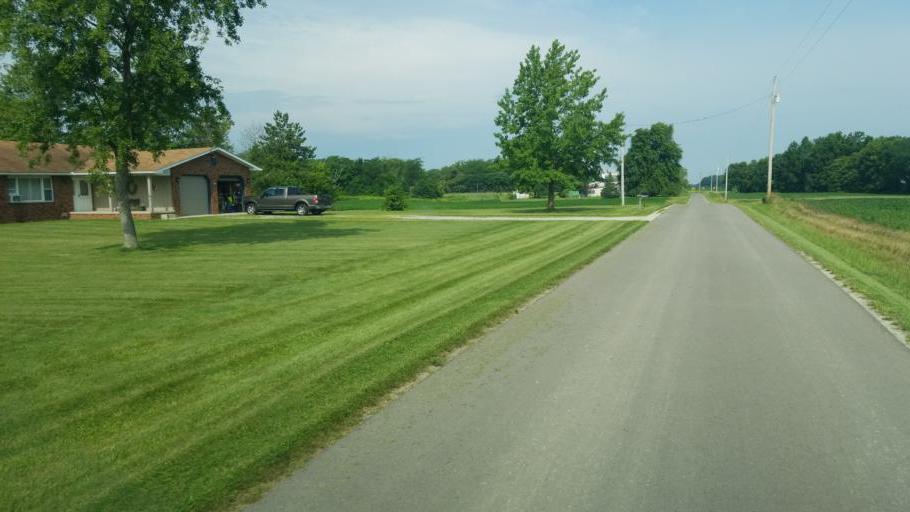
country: US
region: Ohio
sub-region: Wyandot County
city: Upper Sandusky
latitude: 40.6714
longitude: -83.3389
